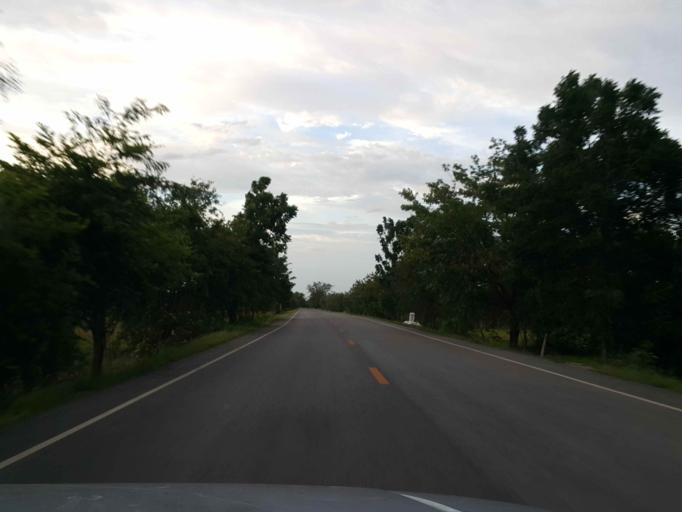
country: TH
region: Sukhothai
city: Ban Dan Lan Hoi
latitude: 17.0652
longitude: 99.5912
